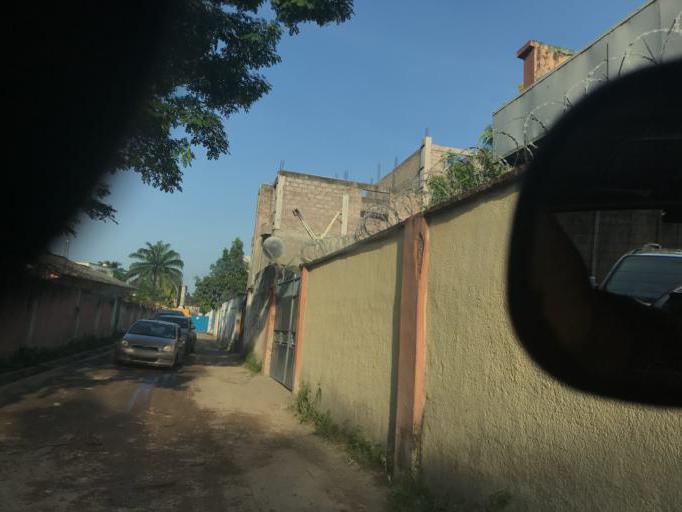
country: CD
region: Kinshasa
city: Kinshasa
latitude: -4.3199
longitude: 15.2862
